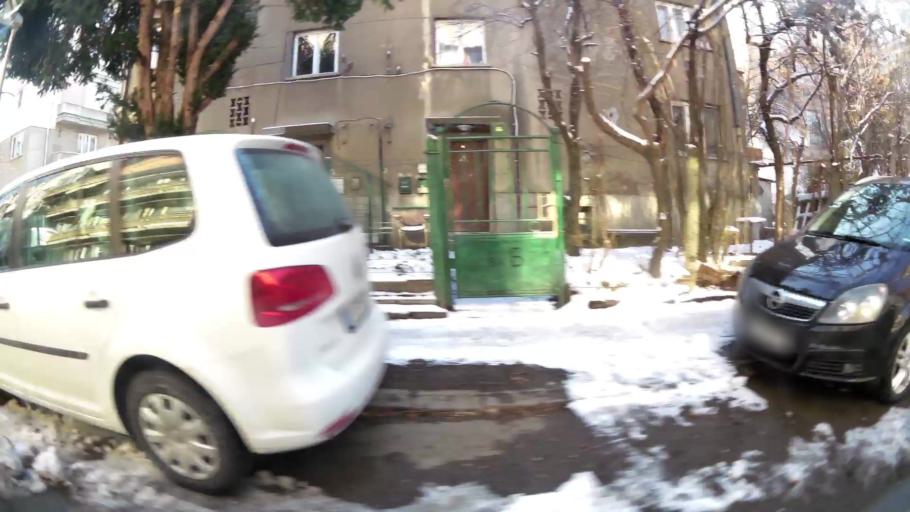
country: BG
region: Sofia-Capital
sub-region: Stolichna Obshtina
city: Sofia
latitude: 42.6729
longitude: 23.3585
